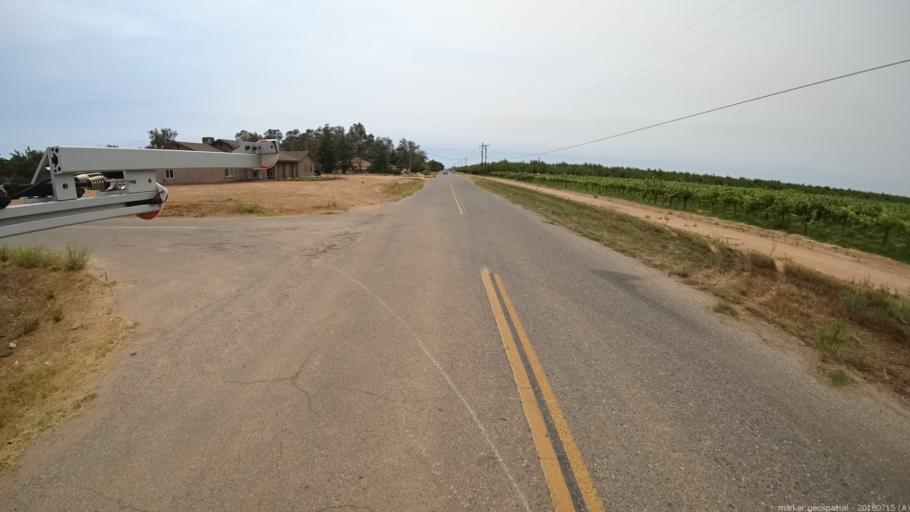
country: US
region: California
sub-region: Madera County
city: Madera Acres
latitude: 37.0109
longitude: -120.0956
